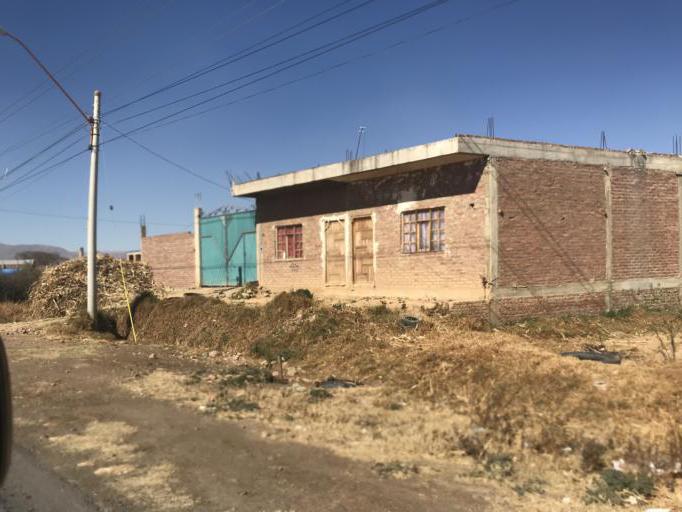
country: BO
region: Cochabamba
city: Cliza
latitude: -17.5723
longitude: -65.8990
